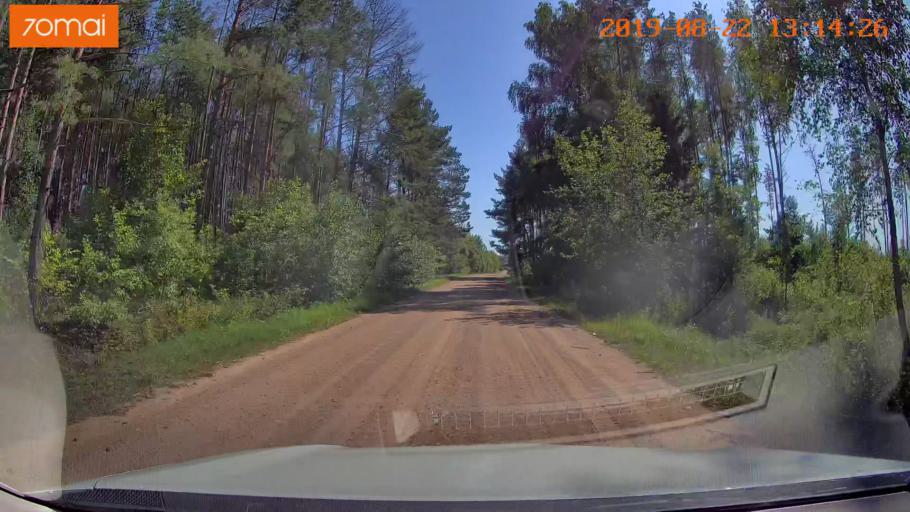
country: BY
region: Minsk
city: Prawdzinski
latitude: 53.2679
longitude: 27.8873
